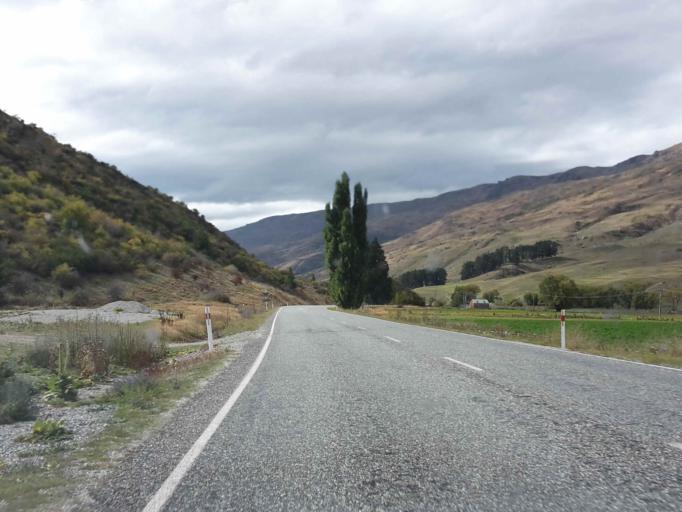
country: NZ
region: Otago
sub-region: Queenstown-Lakes District
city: Wanaka
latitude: -44.8518
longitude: 169.0375
